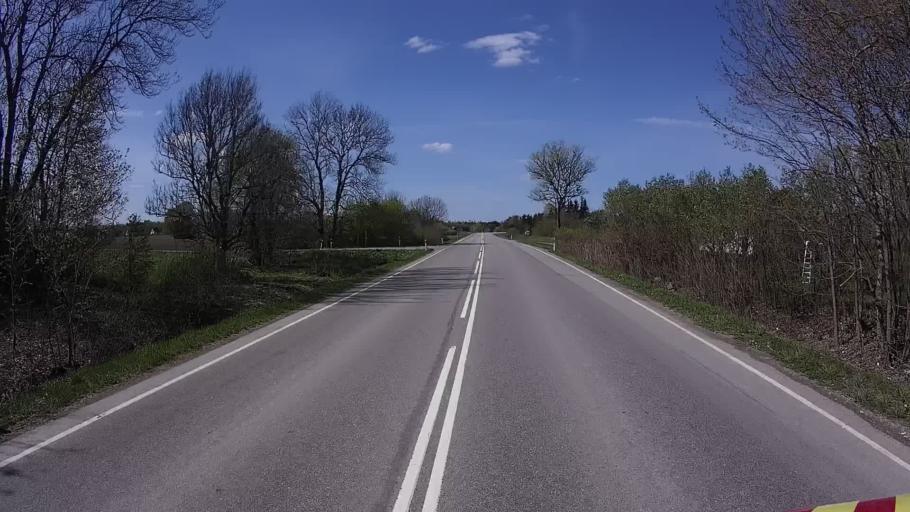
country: EE
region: Harju
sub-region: Keila linn
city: Keila
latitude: 59.2961
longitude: 24.3327
